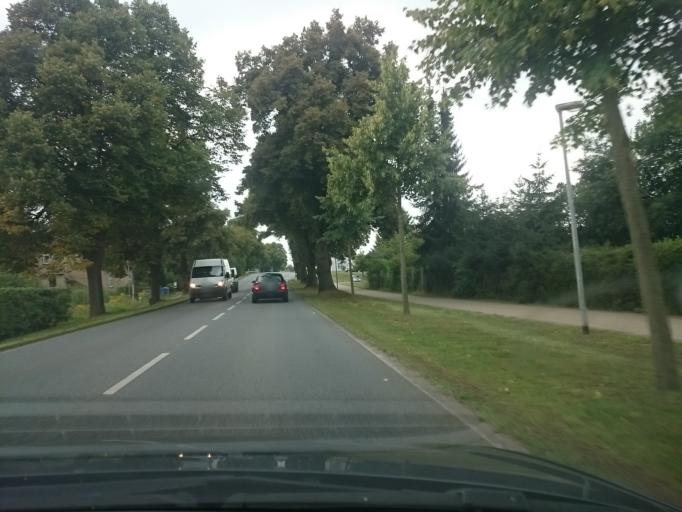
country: DE
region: Brandenburg
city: Furstenberg
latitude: 53.1728
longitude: 13.1430
